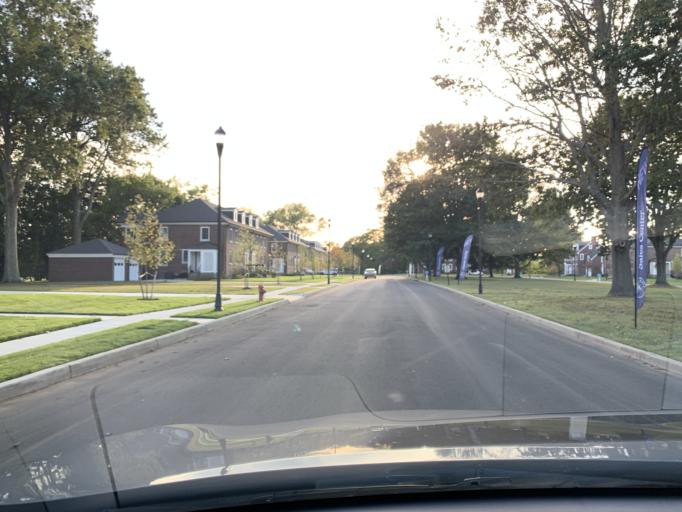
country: US
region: New Jersey
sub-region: Monmouth County
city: Little Silver
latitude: 40.3176
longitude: -74.0399
